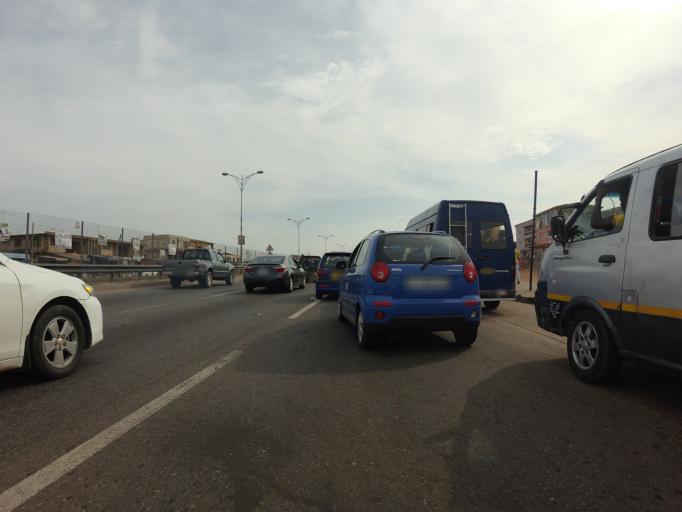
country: GH
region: Greater Accra
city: Dome
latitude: 5.6025
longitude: -0.2587
